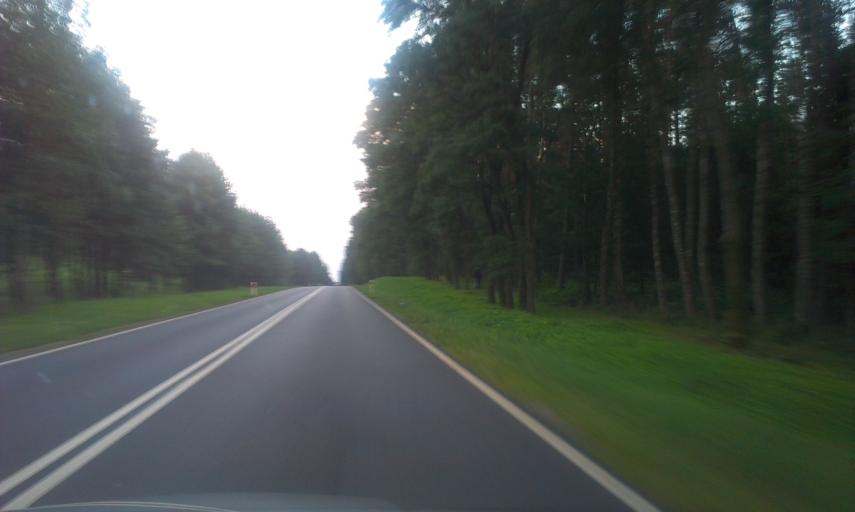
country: PL
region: West Pomeranian Voivodeship
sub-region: Powiat koszalinski
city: Sianow
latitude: 54.0897
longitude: 16.3706
